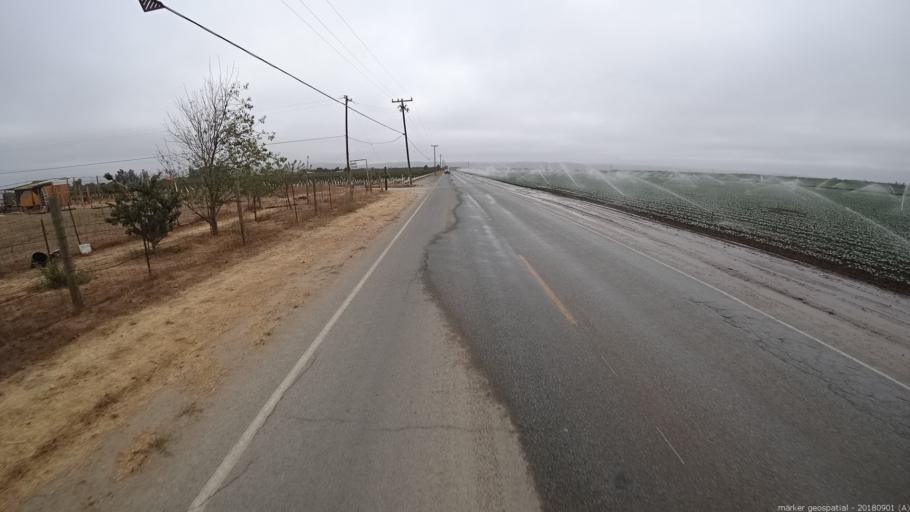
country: US
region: California
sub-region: Monterey County
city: Greenfield
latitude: 36.3003
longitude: -121.2723
